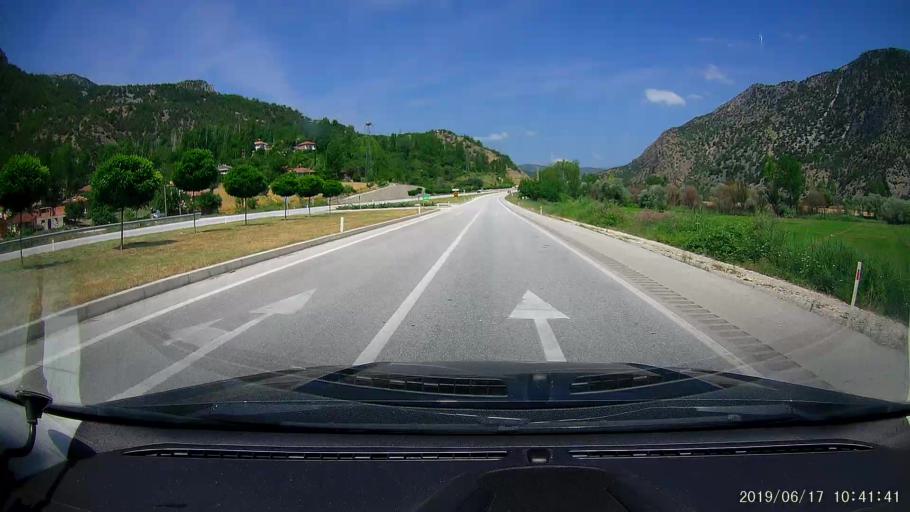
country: TR
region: Corum
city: Kargi
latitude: 41.0421
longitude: 34.5705
